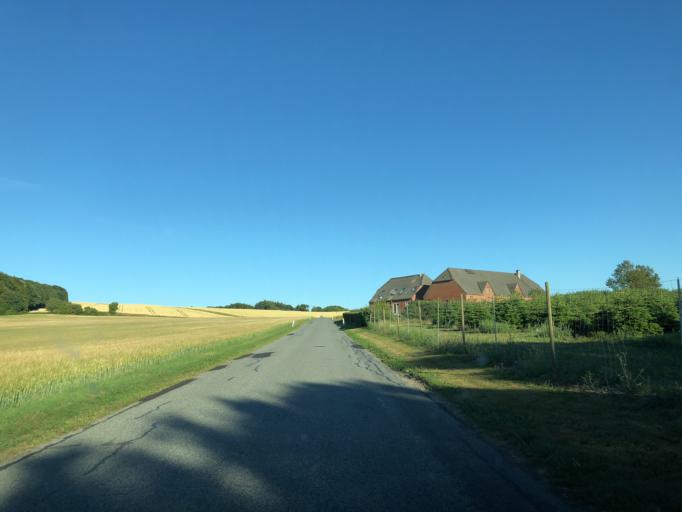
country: DK
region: Central Jutland
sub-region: Skanderborg Kommune
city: Ry
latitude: 55.9940
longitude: 9.7818
